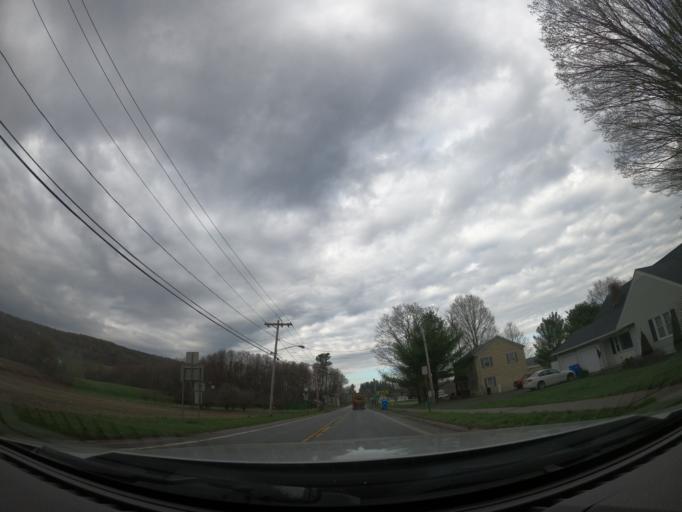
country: US
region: New York
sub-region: Madison County
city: Cazenovia
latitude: 42.7559
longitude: -75.8917
